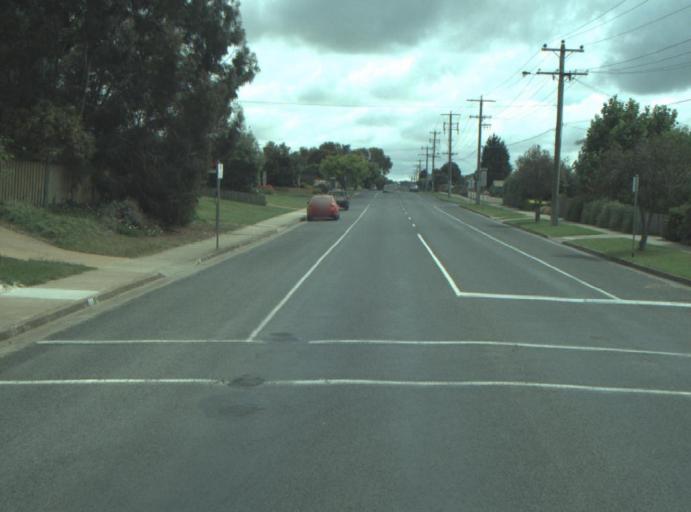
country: AU
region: Victoria
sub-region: Greater Geelong
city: Wandana Heights
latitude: -38.1852
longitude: 144.3104
